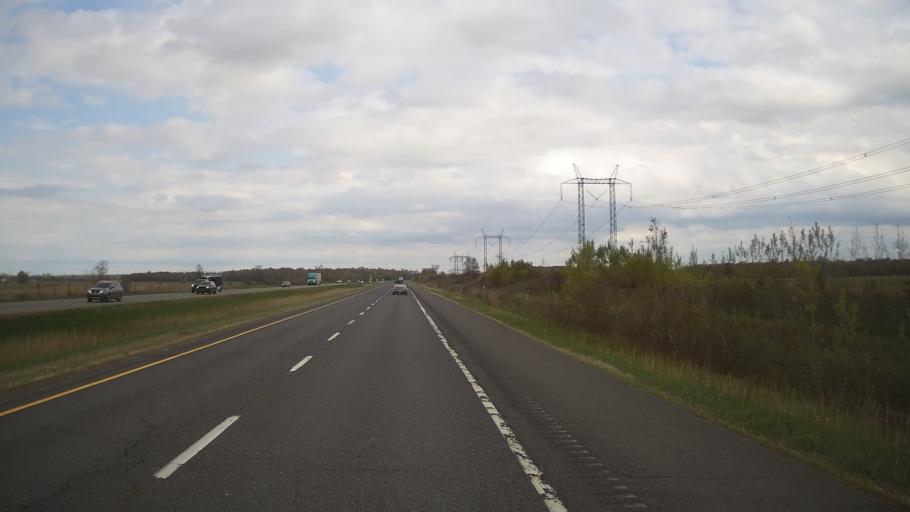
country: CA
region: Quebec
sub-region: Monteregie
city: Saint-Cesaire
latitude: 45.3760
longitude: -72.9813
